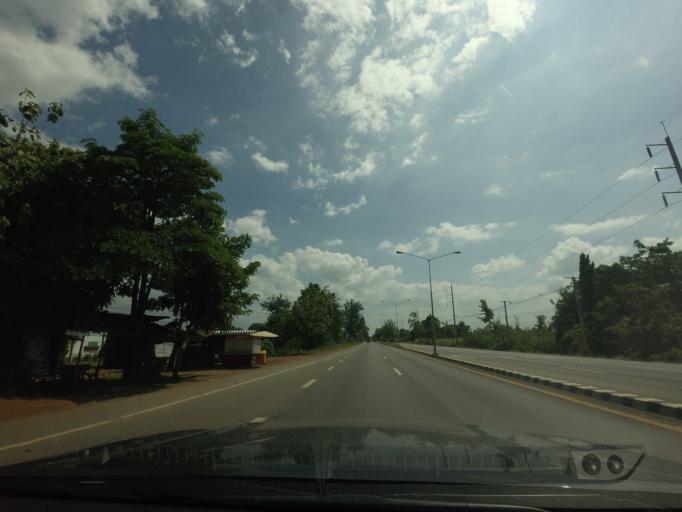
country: TH
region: Phetchabun
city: Nong Phai
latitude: 15.9054
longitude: 101.0274
